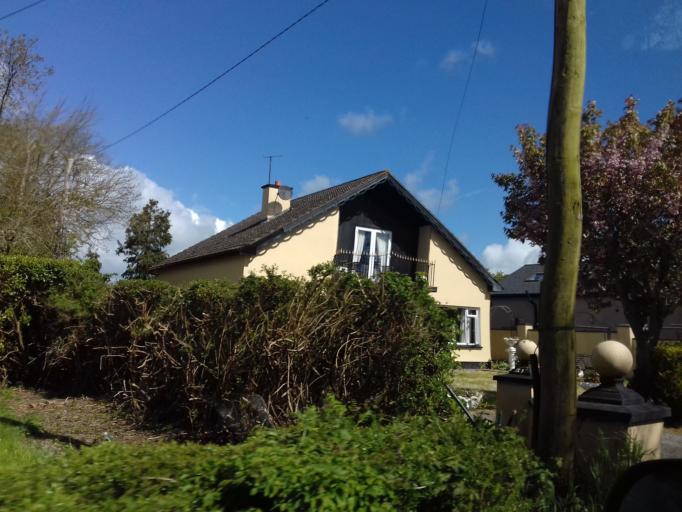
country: IE
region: Leinster
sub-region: Loch Garman
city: Castlebridge
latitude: 52.3710
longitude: -6.4352
